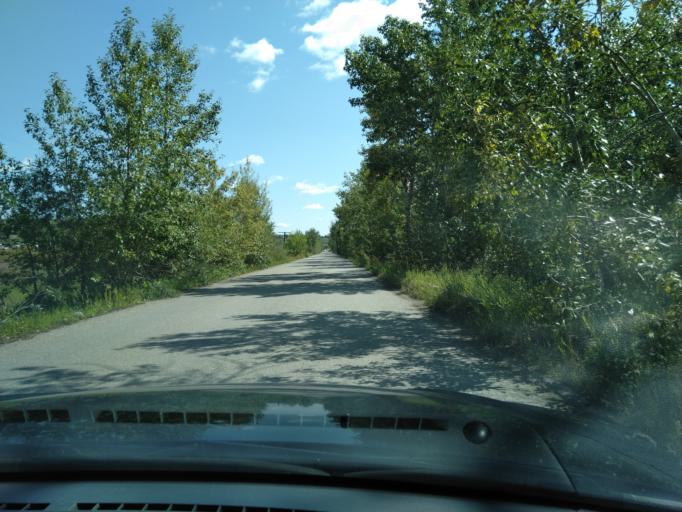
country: CA
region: Alberta
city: Calgary
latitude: 51.1016
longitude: -114.2192
